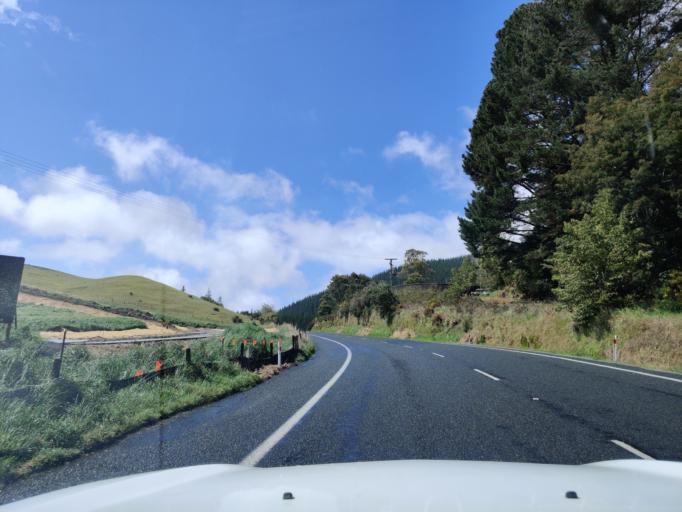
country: NZ
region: Bay of Plenty
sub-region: Rotorua District
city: Rotorua
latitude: -38.1596
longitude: 176.2979
